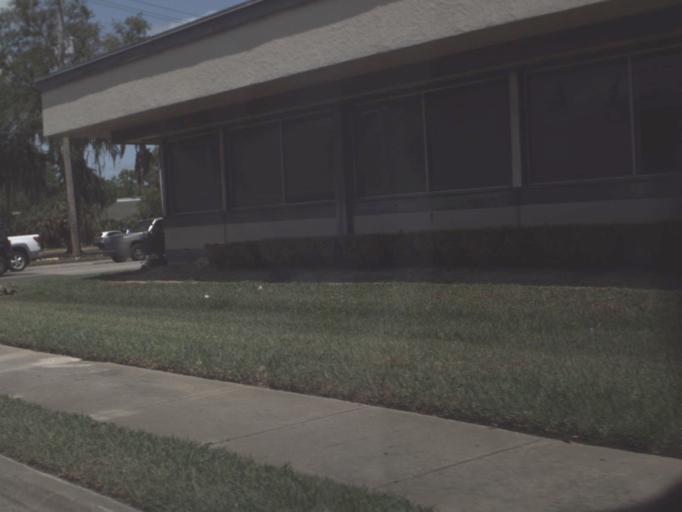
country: US
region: Florida
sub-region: Marion County
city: Ocala
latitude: 29.1870
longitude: -82.1161
